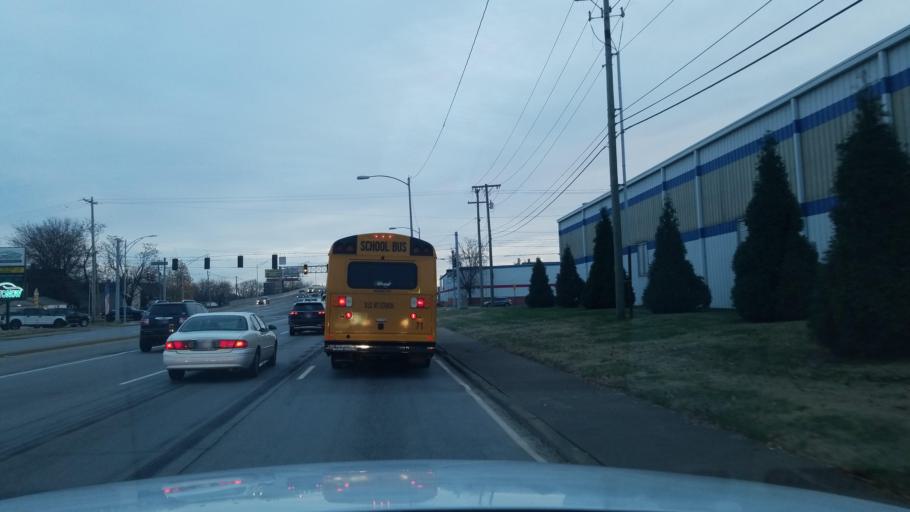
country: US
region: Indiana
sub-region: Vanderburgh County
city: Evansville
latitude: 37.9777
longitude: -87.5951
